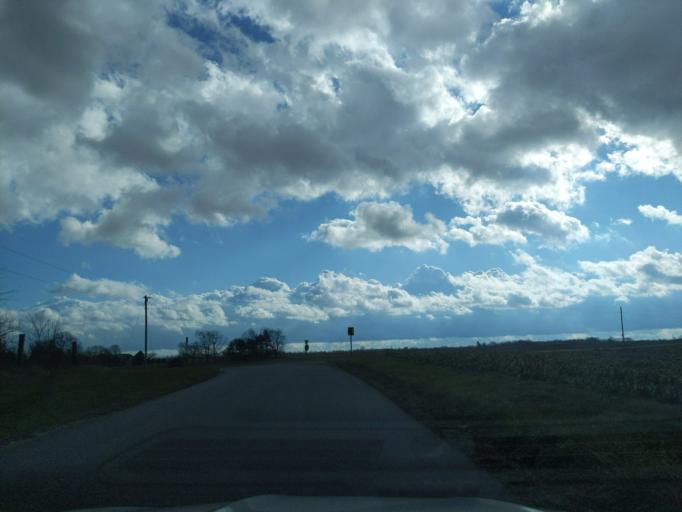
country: US
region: Indiana
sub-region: Decatur County
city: Greensburg
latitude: 39.4099
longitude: -85.5083
